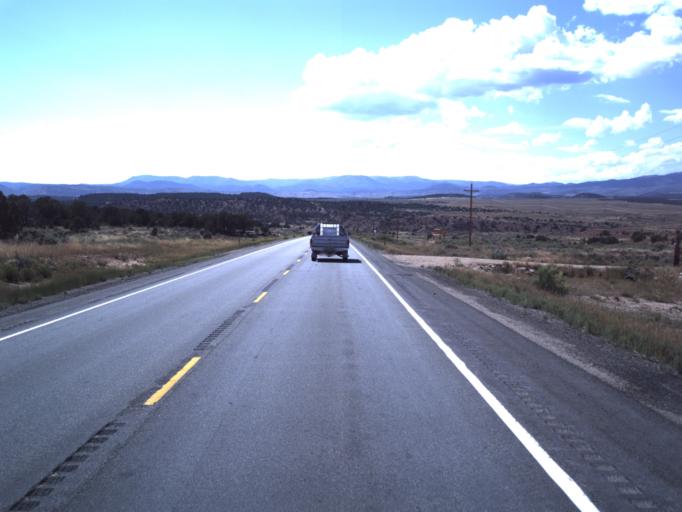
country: US
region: Utah
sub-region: Duchesne County
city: Duchesne
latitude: 40.2091
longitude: -110.7464
